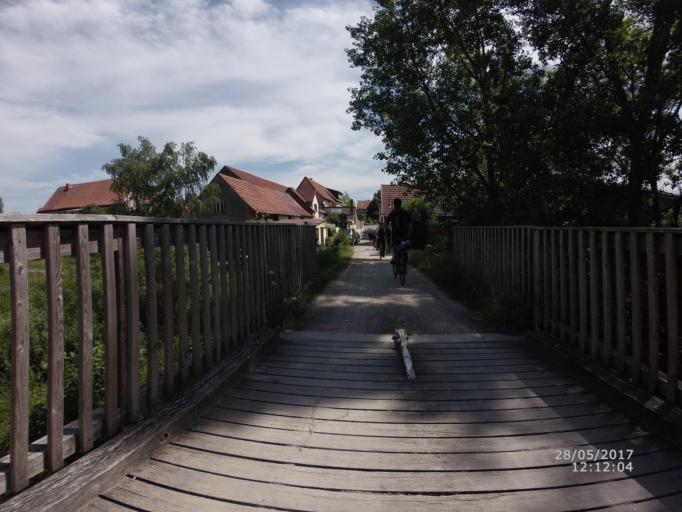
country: DE
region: Thuringia
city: Etzleben
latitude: 51.2615
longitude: 11.1717
